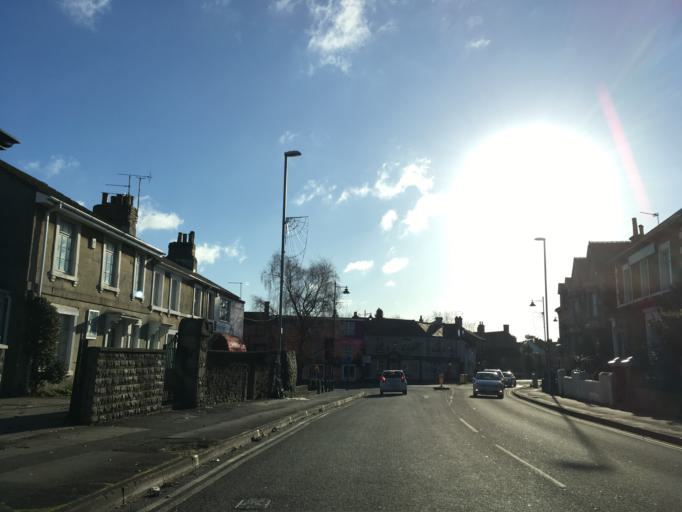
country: GB
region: England
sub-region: Borough of Swindon
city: Swindon
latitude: 51.5505
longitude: -1.7770
